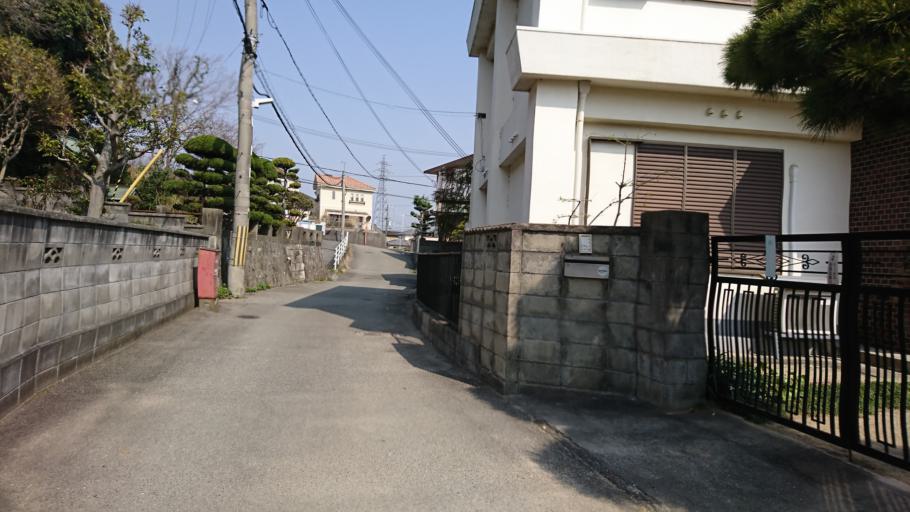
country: JP
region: Hyogo
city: Shirahamacho-usazakiminami
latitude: 34.7938
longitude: 134.7614
